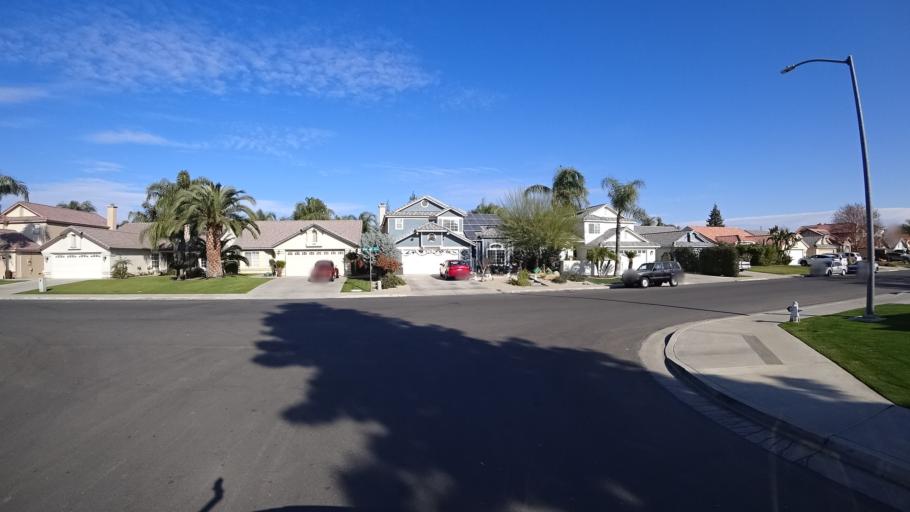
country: US
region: California
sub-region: Kern County
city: Greenacres
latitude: 35.4051
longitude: -119.0976
